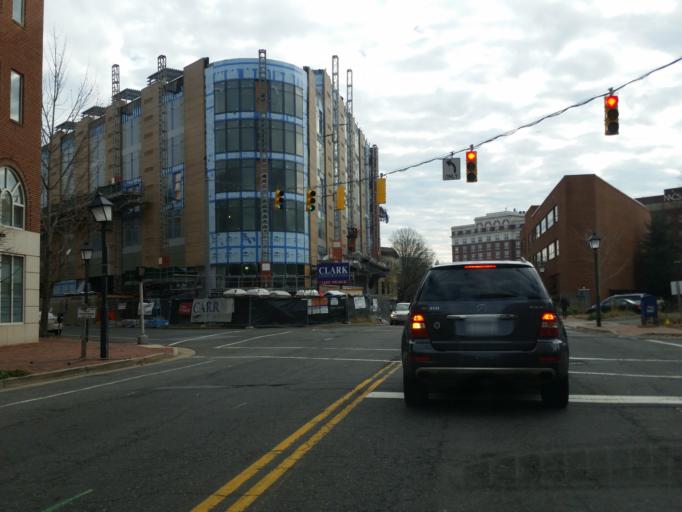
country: US
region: Virginia
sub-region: City of Alexandria
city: Alexandria
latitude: 38.8056
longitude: -77.0589
